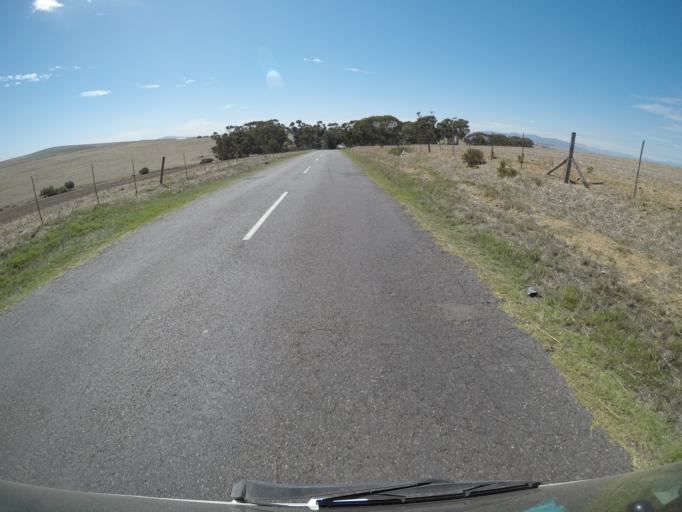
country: ZA
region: Western Cape
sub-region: City of Cape Town
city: Atlantis
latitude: -33.7018
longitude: 18.5876
